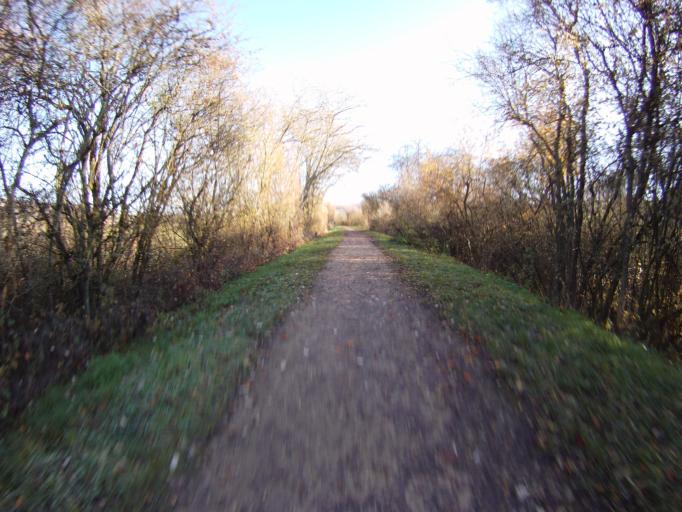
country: FR
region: Lorraine
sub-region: Departement de Meurthe-et-Moselle
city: Faulx
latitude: 48.7910
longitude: 6.2219
